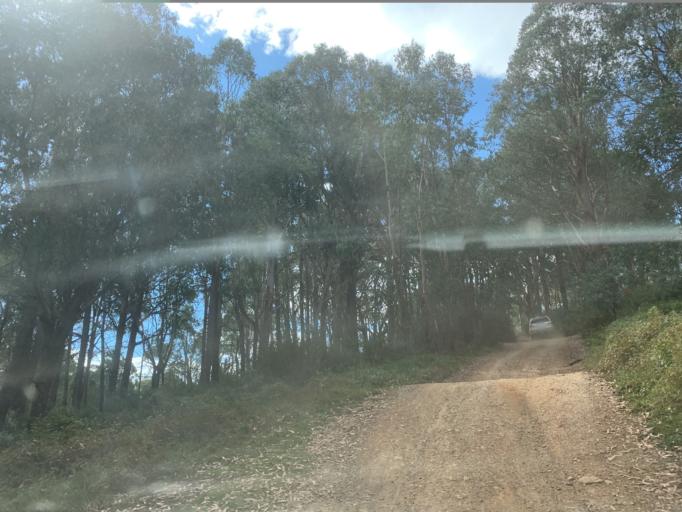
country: AU
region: Victoria
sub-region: Mansfield
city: Mansfield
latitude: -37.1051
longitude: 146.5357
